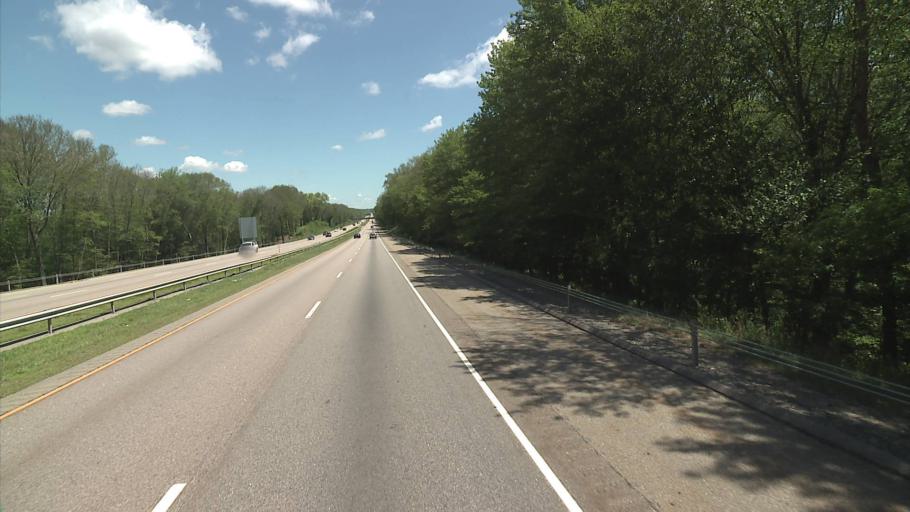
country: US
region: Connecticut
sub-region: New London County
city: Oxoboxo River
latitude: 41.4071
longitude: -72.1459
